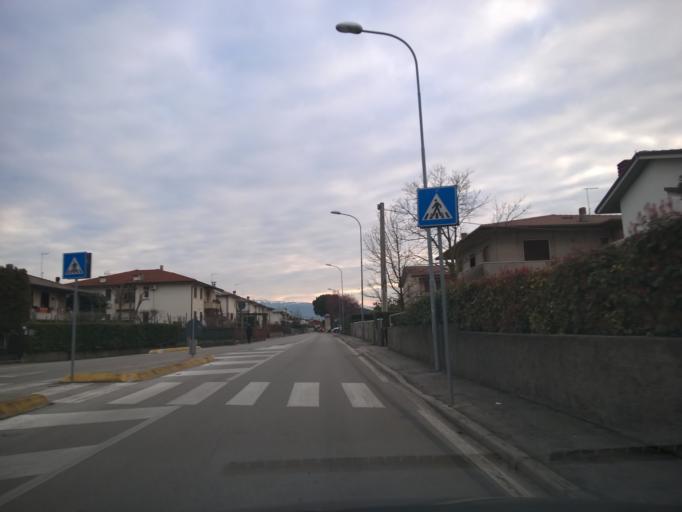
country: IT
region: Veneto
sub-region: Provincia di Vicenza
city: Thiene
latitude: 45.6979
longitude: 11.4886
